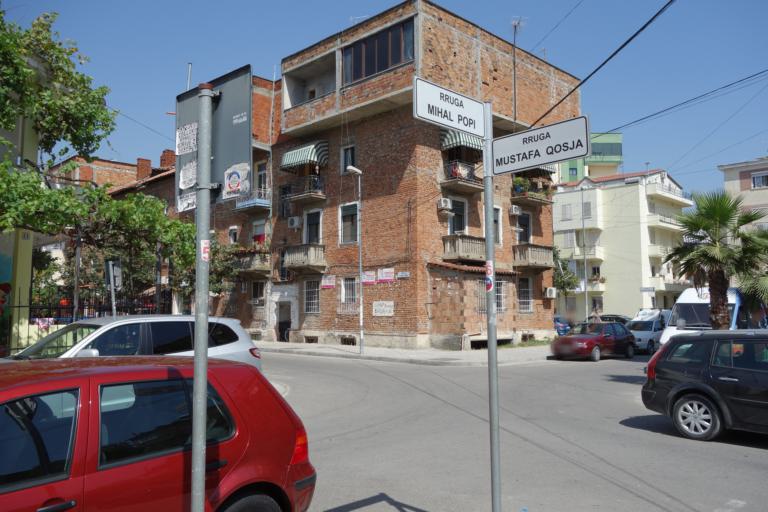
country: AL
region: Tirane
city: Tirana
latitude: 41.3203
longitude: 19.8086
